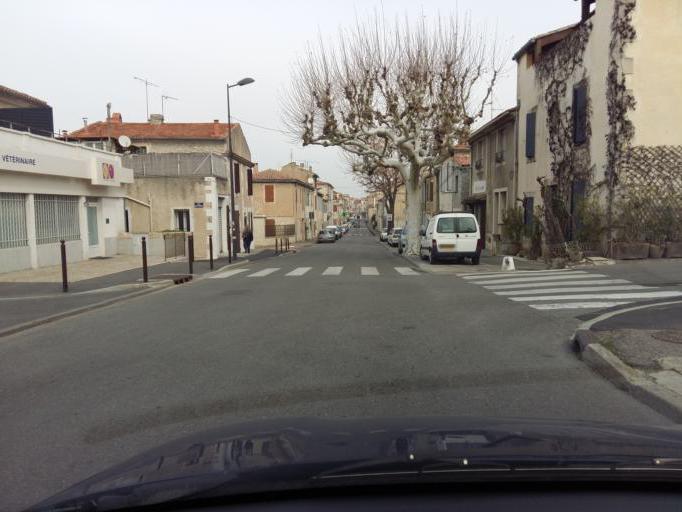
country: FR
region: Provence-Alpes-Cote d'Azur
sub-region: Departement des Bouches-du-Rhone
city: Chateaurenard
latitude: 43.8788
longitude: 4.8532
